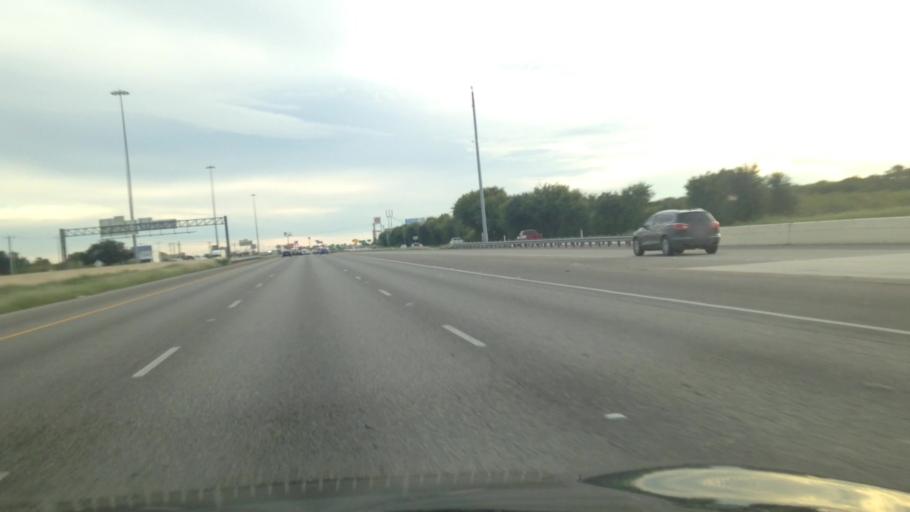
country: US
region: Texas
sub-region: Hays County
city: Buda
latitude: 30.1008
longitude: -97.8127
